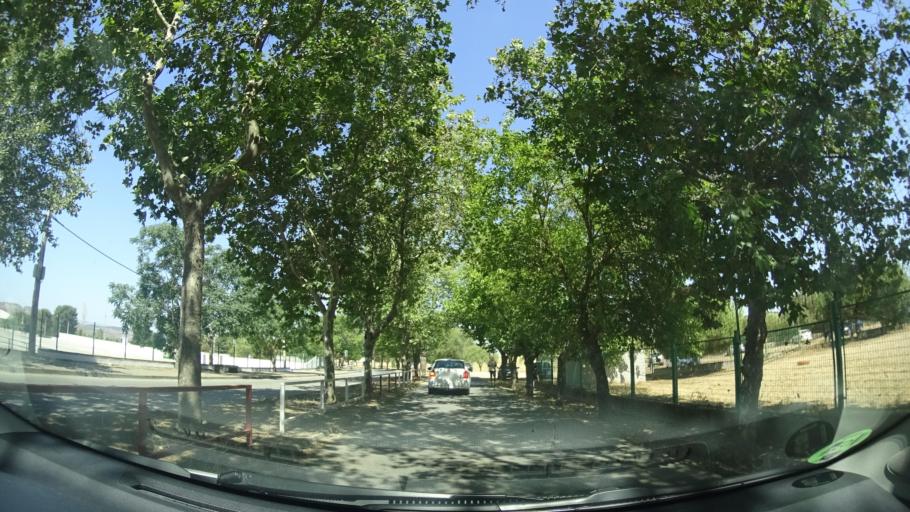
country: ES
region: Extremadura
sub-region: Provincia de Badajoz
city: Zafra
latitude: 38.4306
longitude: -6.4058
